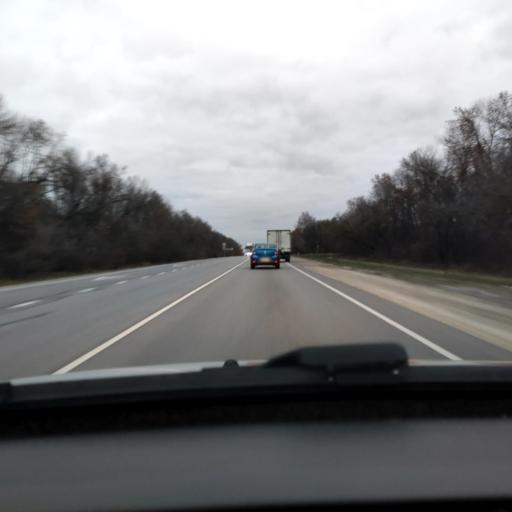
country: RU
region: Lipetsk
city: Borinskoye
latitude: 52.3902
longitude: 39.2281
